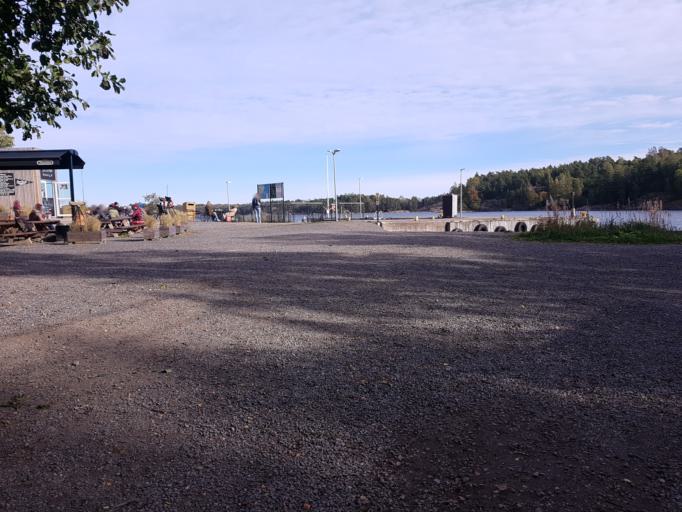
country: FI
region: Uusimaa
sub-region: Helsinki
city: Helsinki
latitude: 60.1376
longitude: 25.0091
